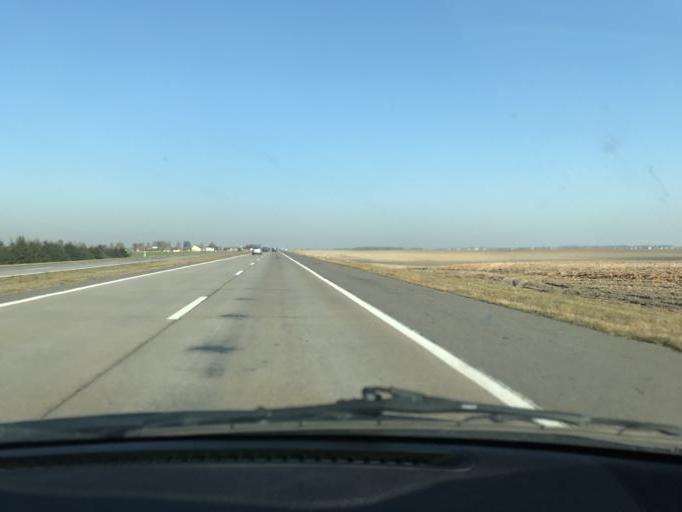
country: BY
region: Minsk
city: Samakhvalavichy
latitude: 53.6678
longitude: 27.4901
